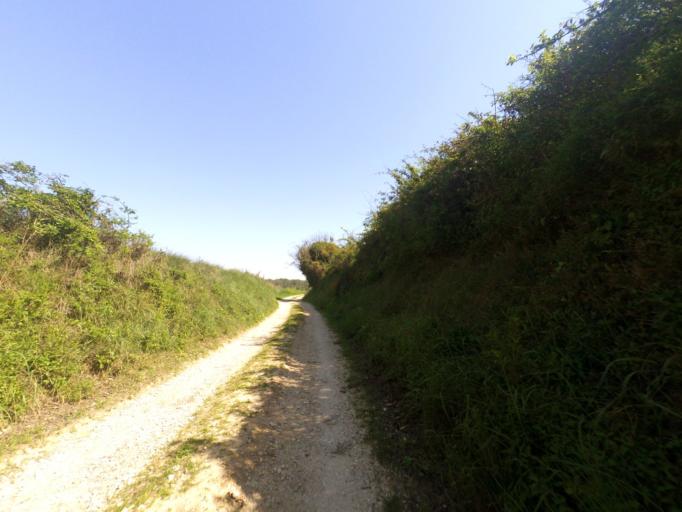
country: FR
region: Languedoc-Roussillon
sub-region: Departement du Gard
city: Calvisson
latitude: 43.7645
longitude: 4.1967
